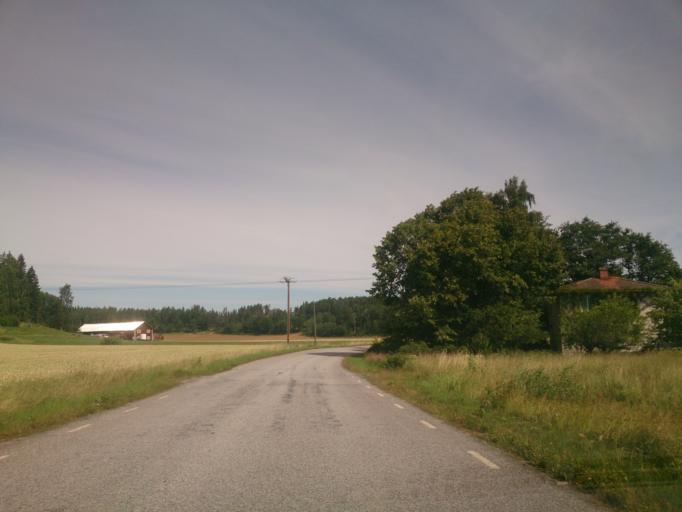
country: SE
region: OEstergoetland
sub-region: Valdemarsviks Kommun
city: Gusum
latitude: 58.3429
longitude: 16.5905
